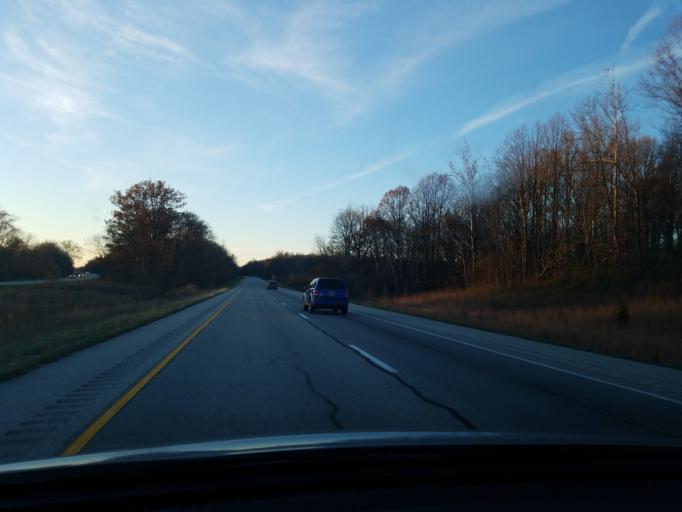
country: US
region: Indiana
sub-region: Posey County
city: Poseyville
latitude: 38.1922
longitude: -87.8379
